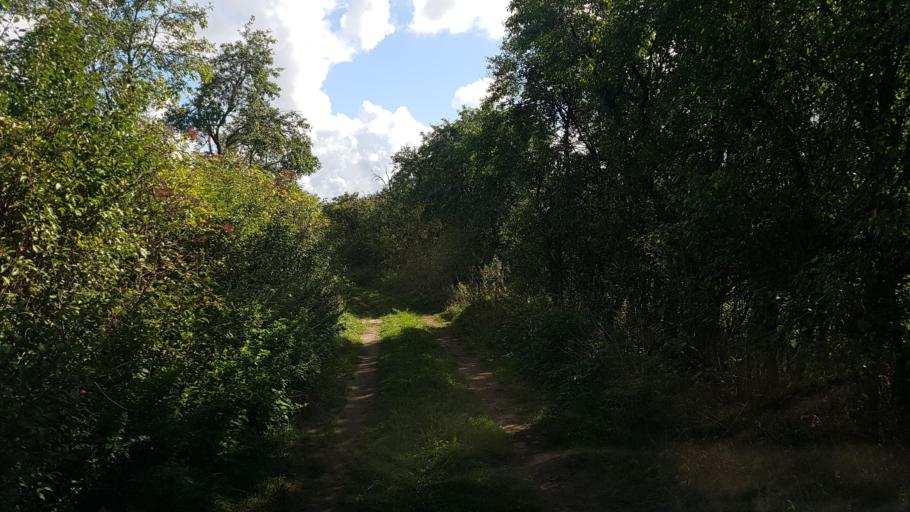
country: DE
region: Brandenburg
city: Niemegk
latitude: 52.0710
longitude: 12.7572
